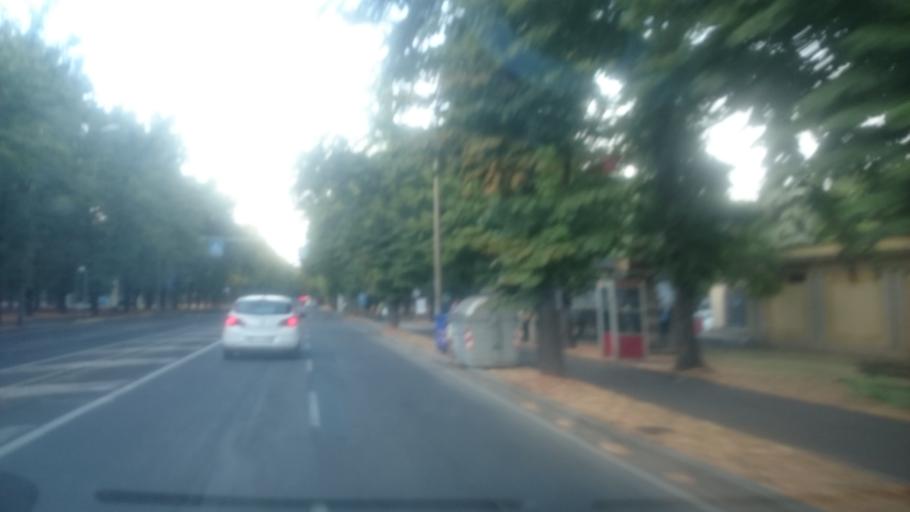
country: IT
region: Emilia-Romagna
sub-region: Provincia di Reggio Emilia
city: Reggio nell'Emilia
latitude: 44.6851
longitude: 10.6241
